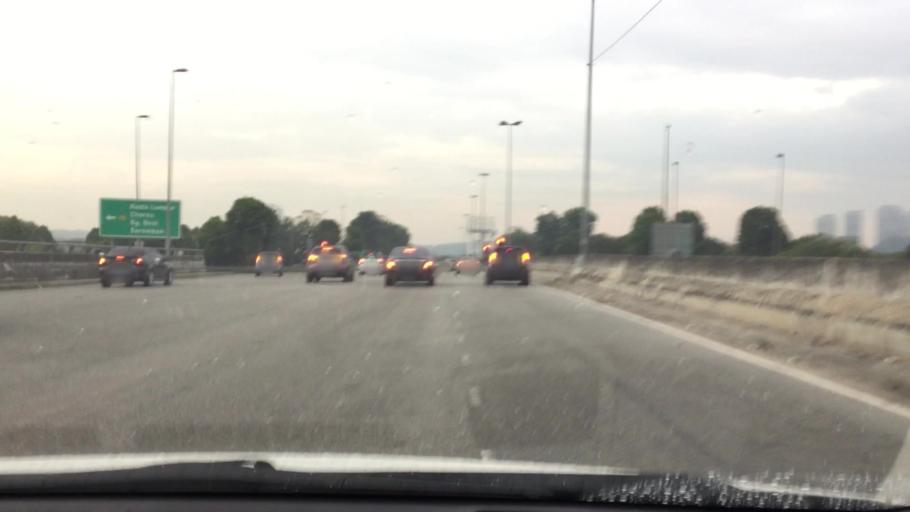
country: MY
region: Selangor
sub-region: Petaling
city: Petaling Jaya
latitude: 3.0707
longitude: 101.6415
